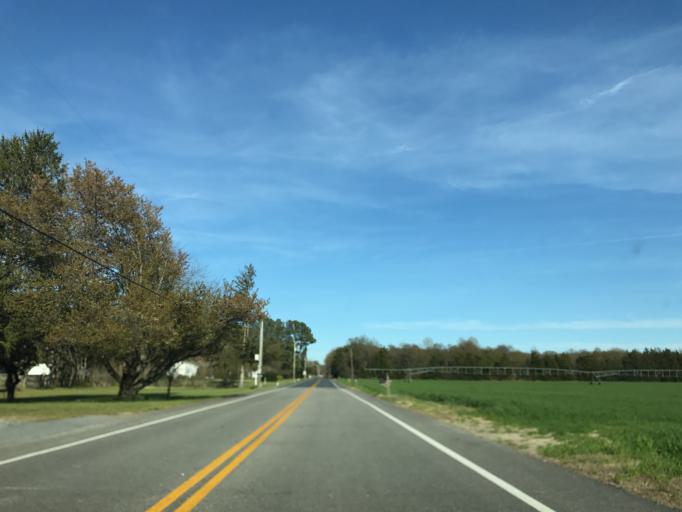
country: US
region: Maryland
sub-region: Caroline County
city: Greensboro
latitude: 39.0288
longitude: -75.7520
